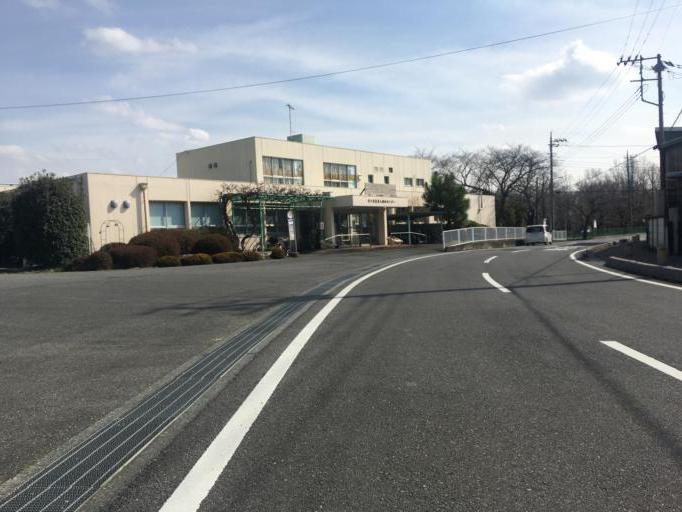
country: JP
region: Saitama
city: Kamifukuoka
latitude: 35.8811
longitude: 139.5557
